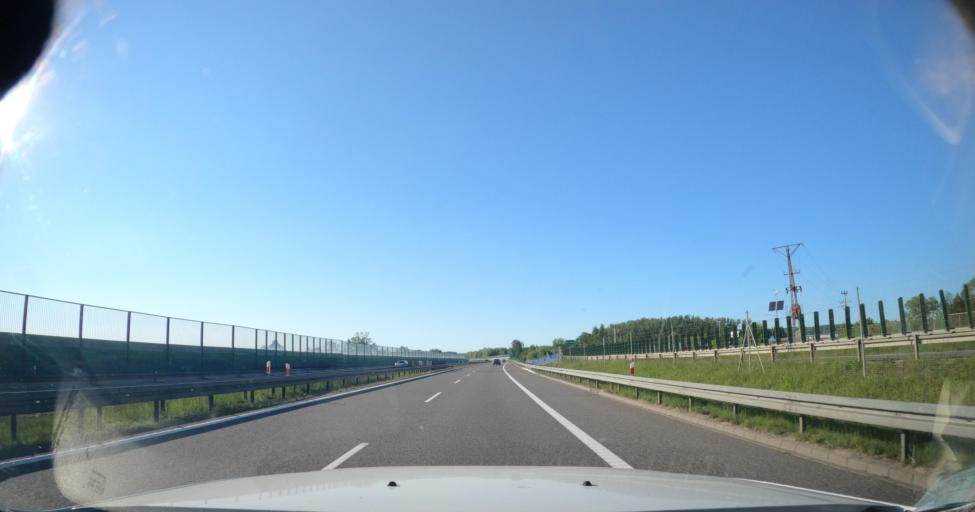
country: PL
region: Warmian-Masurian Voivodeship
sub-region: Powiat elblaski
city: Gronowo Gorne
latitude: 54.1270
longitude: 19.4608
